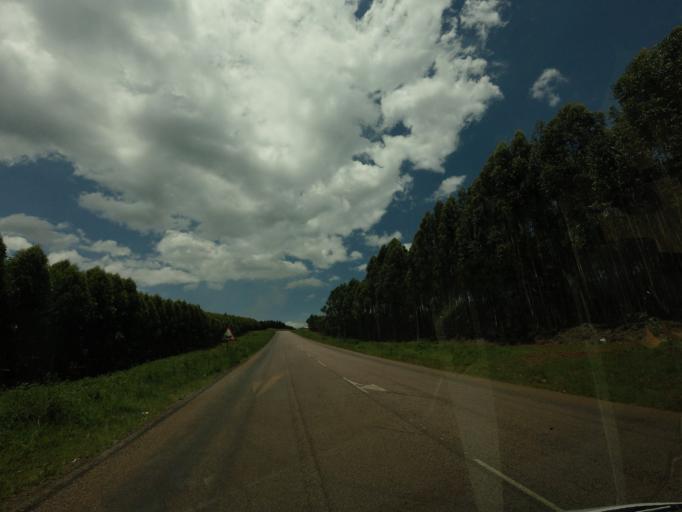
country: ZA
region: Mpumalanga
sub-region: Ehlanzeni District
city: Graksop
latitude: -25.0711
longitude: 30.8034
